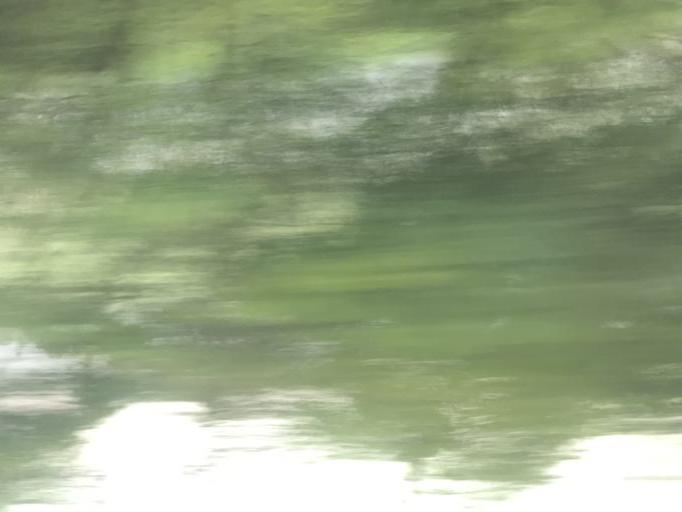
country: IN
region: Andhra Pradesh
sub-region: Guntur
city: Ponnur
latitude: 16.1073
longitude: 80.5753
